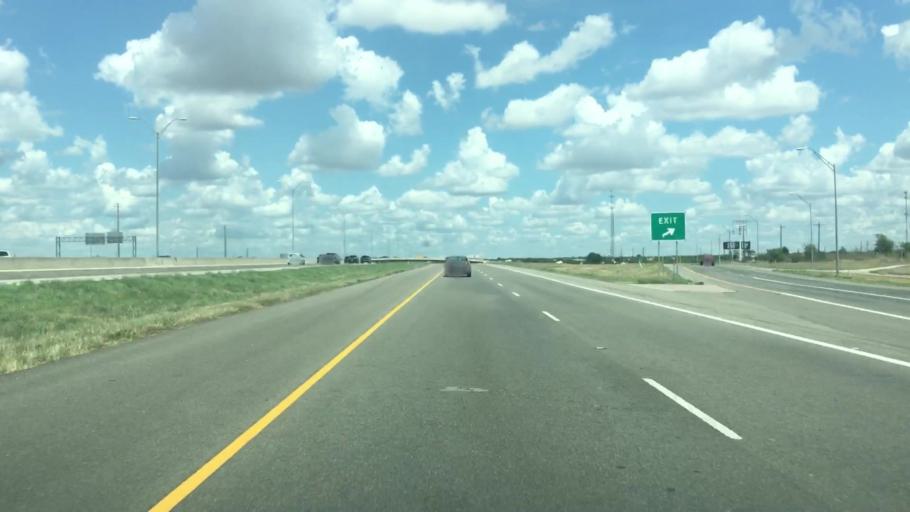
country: US
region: Texas
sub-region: Williamson County
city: Serenada
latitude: 30.6959
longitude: -97.6538
